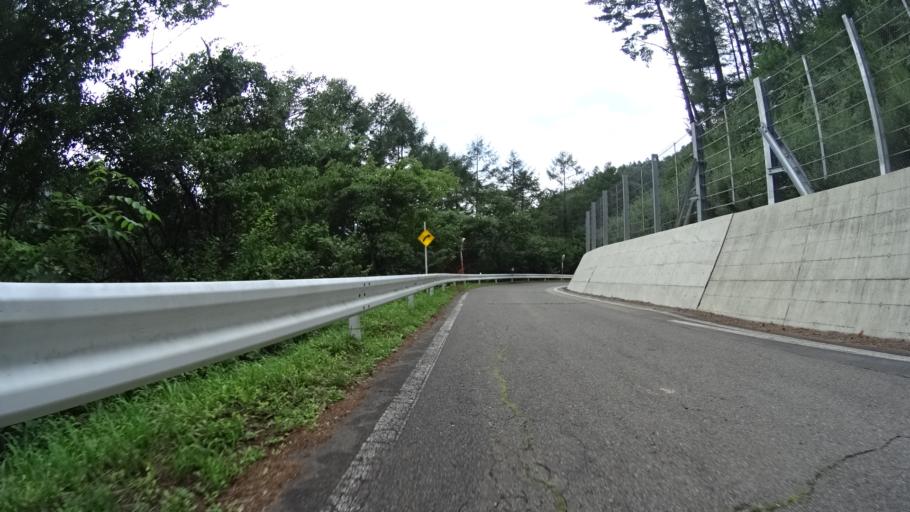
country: JP
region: Nagano
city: Saku
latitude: 36.0702
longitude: 138.6365
